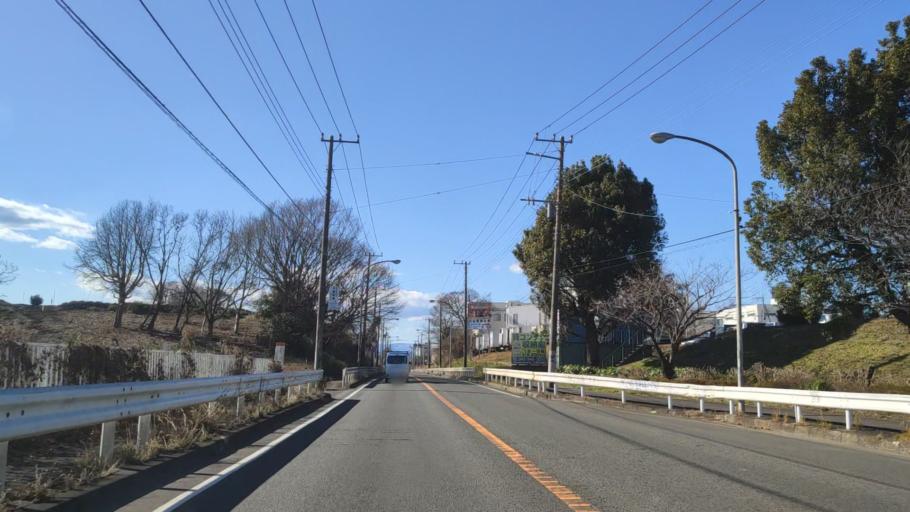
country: JP
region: Kanagawa
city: Minami-rinkan
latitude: 35.4978
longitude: 139.4901
